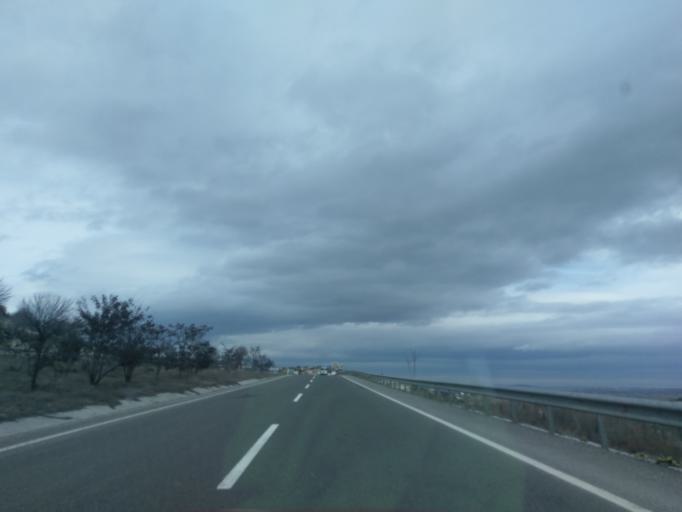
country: TR
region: Kuetahya
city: Kutahya
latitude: 39.3700
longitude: 30.0678
